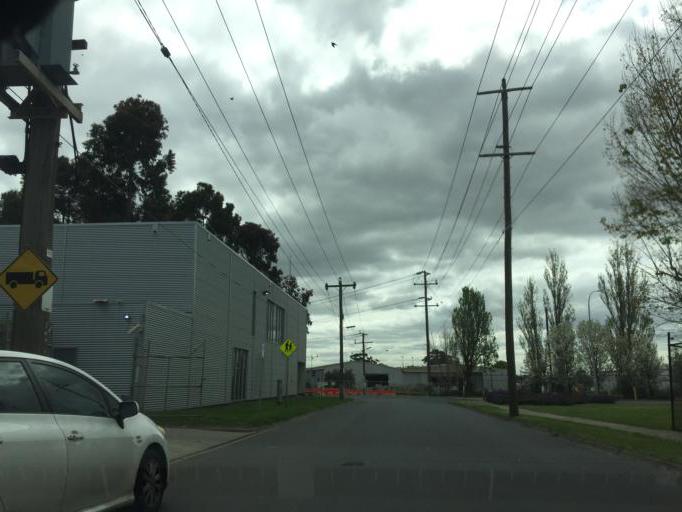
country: AU
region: Victoria
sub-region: Hobsons Bay
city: South Kingsville
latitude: -37.8203
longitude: 144.8601
